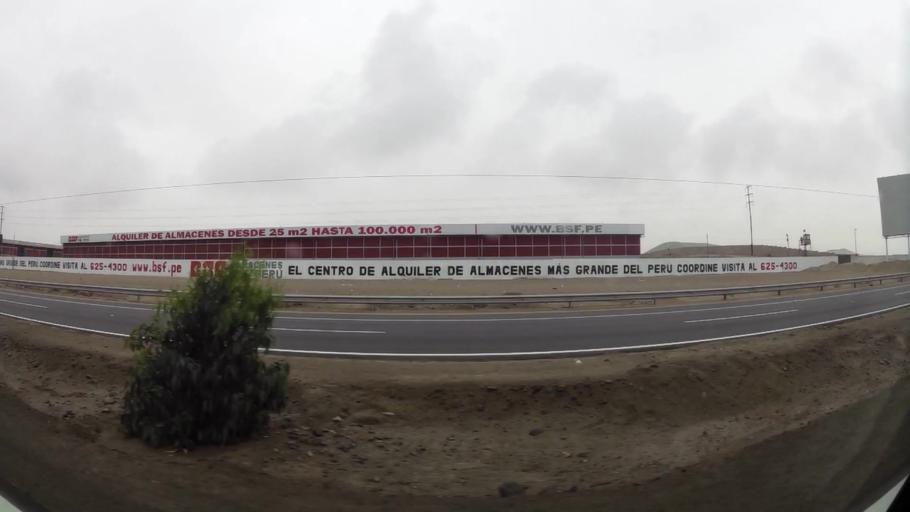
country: PE
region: Lima
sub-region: Lima
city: Punta Hermosa
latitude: -12.3211
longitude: -76.8282
